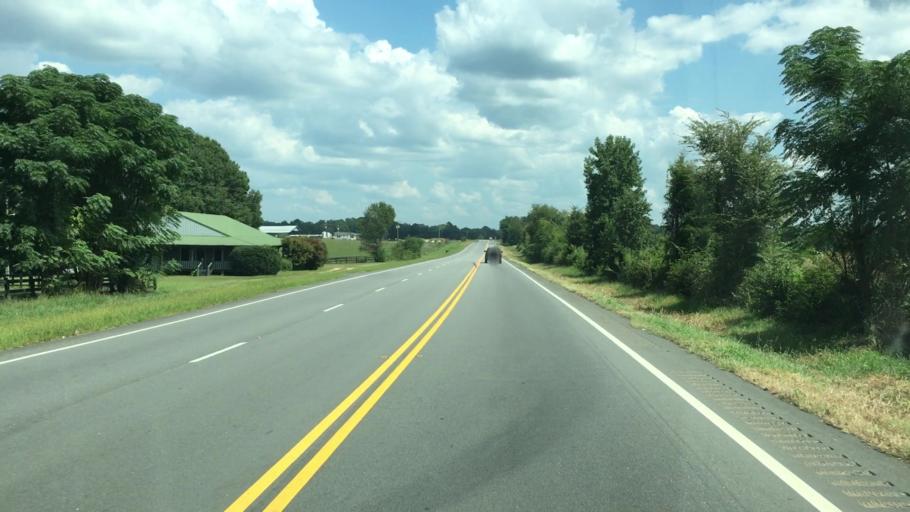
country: US
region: Georgia
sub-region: Putnam County
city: Jefferson
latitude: 33.4748
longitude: -83.4299
